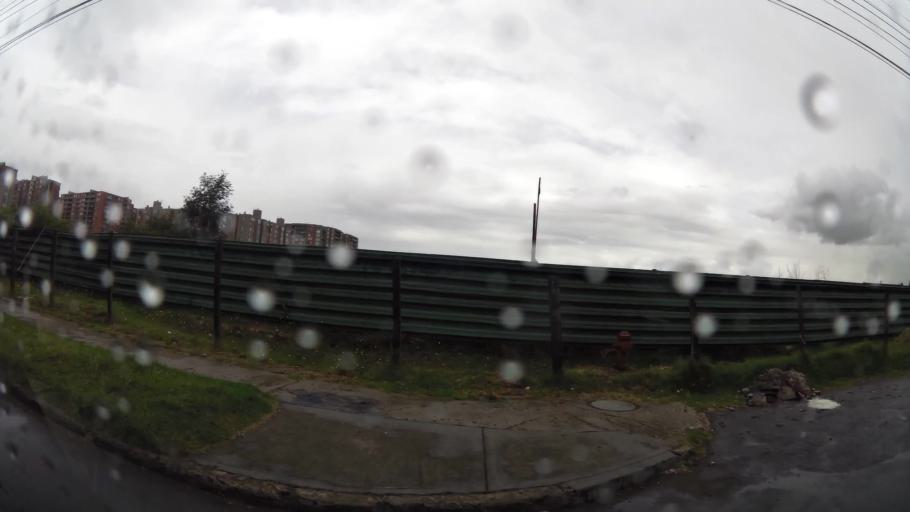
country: CO
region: Bogota D.C.
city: Bogota
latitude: 4.6610
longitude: -74.1204
